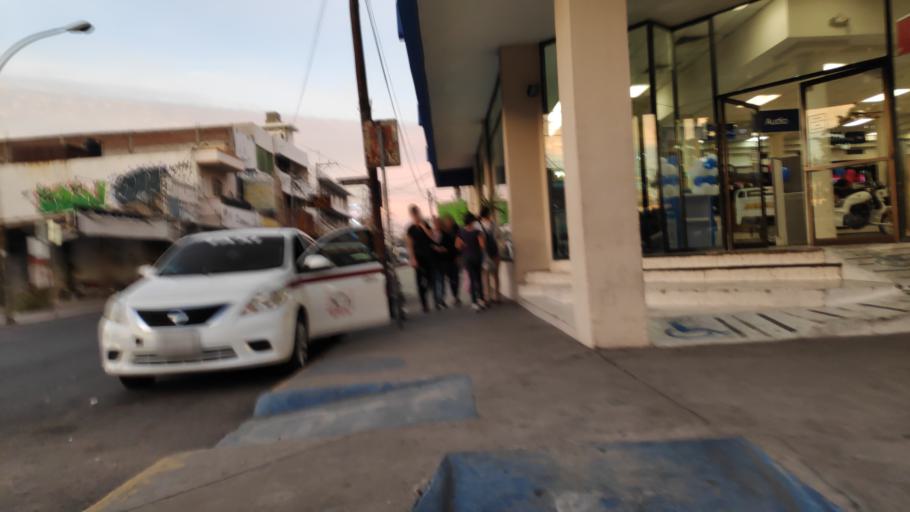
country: MX
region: Sinaloa
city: Culiacan
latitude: 24.8046
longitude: -107.3959
